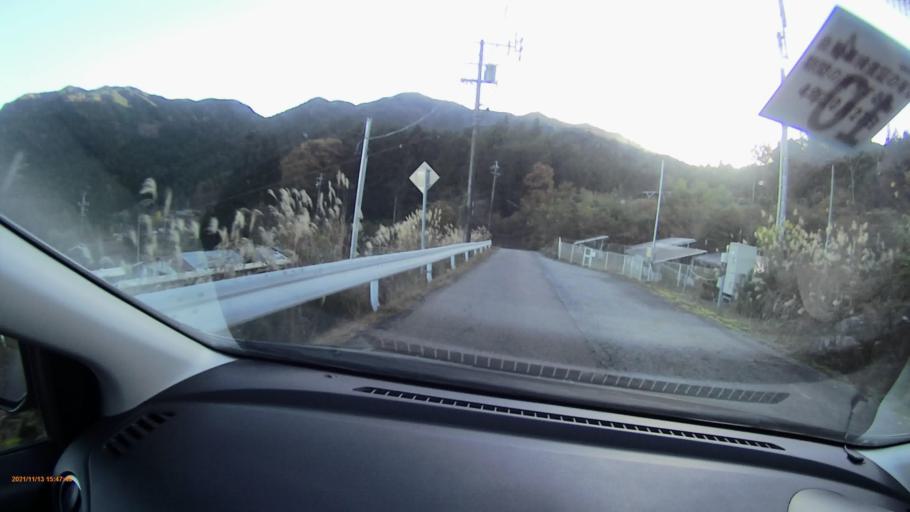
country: JP
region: Gifu
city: Nakatsugawa
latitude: 35.5969
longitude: 137.4034
